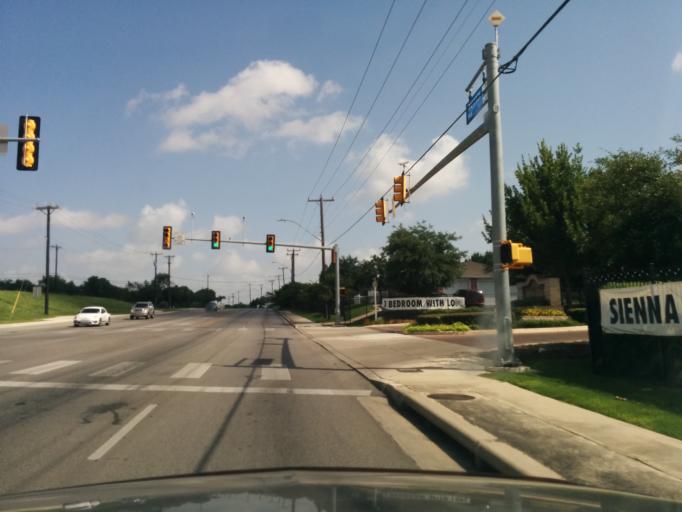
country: US
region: Texas
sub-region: Bexar County
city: Leon Valley
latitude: 29.5273
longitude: -98.6016
